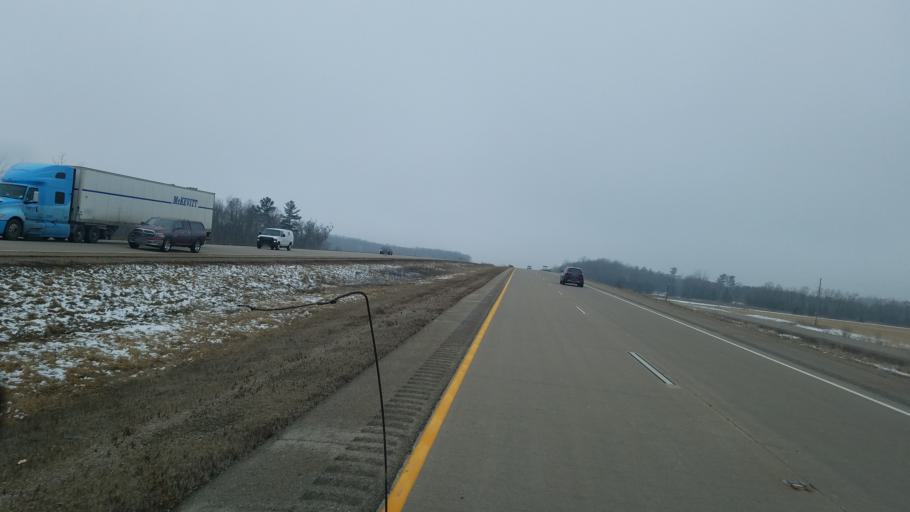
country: US
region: Wisconsin
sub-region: Winnebago County
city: Winneconne
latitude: 44.2342
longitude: -88.7610
